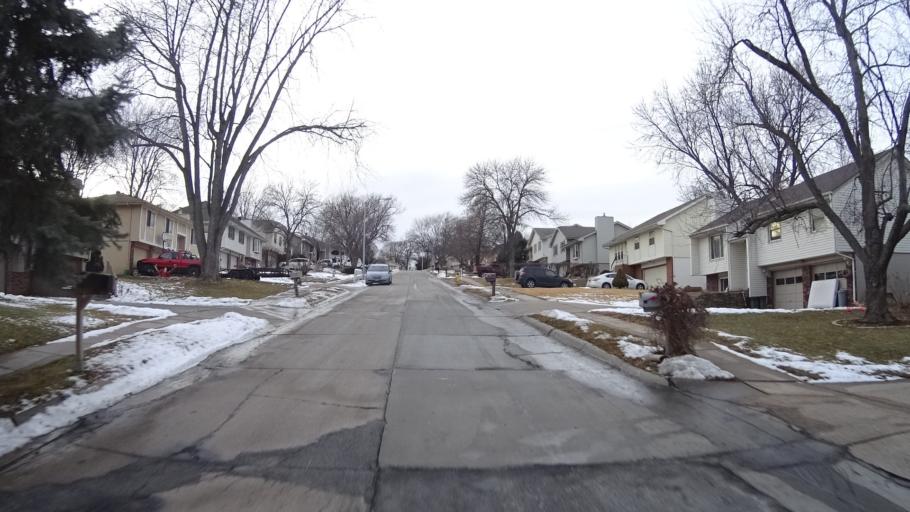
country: US
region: Nebraska
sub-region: Sarpy County
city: Offutt Air Force Base
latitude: 41.1651
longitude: -95.9437
